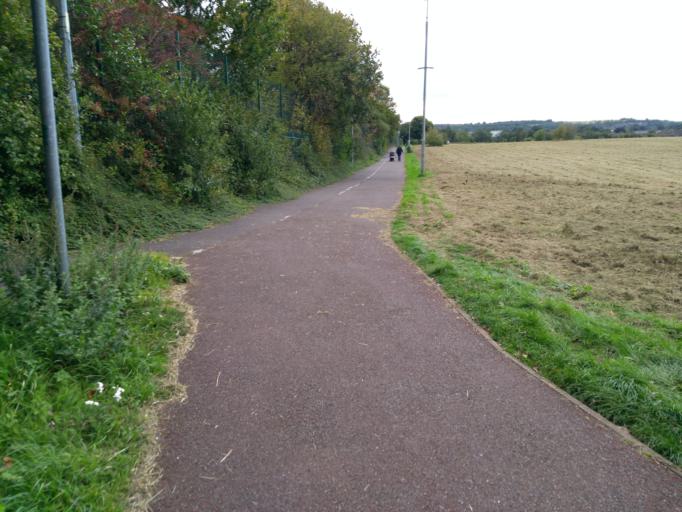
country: GB
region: England
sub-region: Central Bedfordshire
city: Houghton Regis
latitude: 51.8955
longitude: -0.5219
